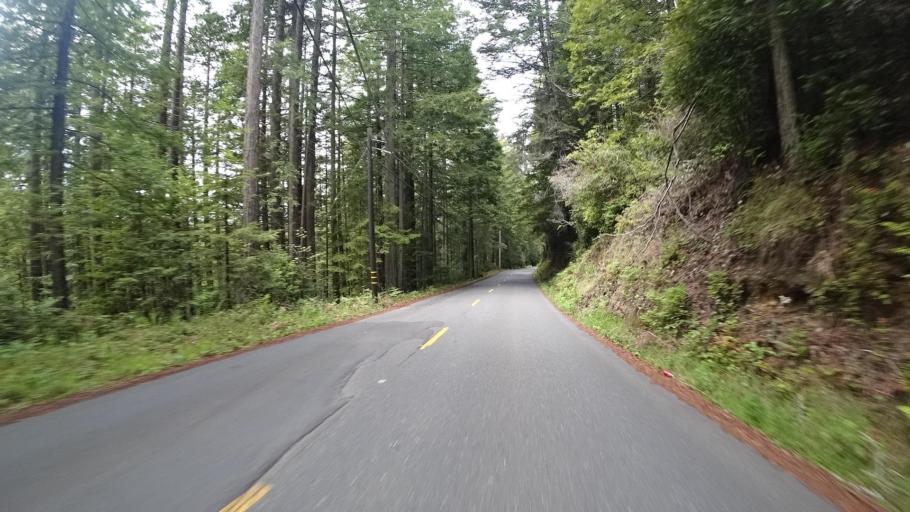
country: US
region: California
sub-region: Humboldt County
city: Myrtletown
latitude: 40.7856
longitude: -124.0746
